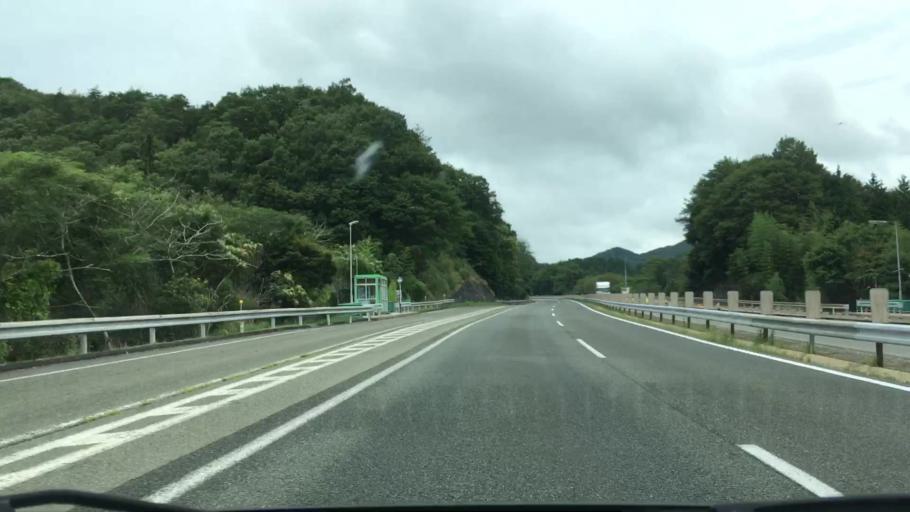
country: JP
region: Hiroshima
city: Shobara
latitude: 34.8718
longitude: 133.1651
